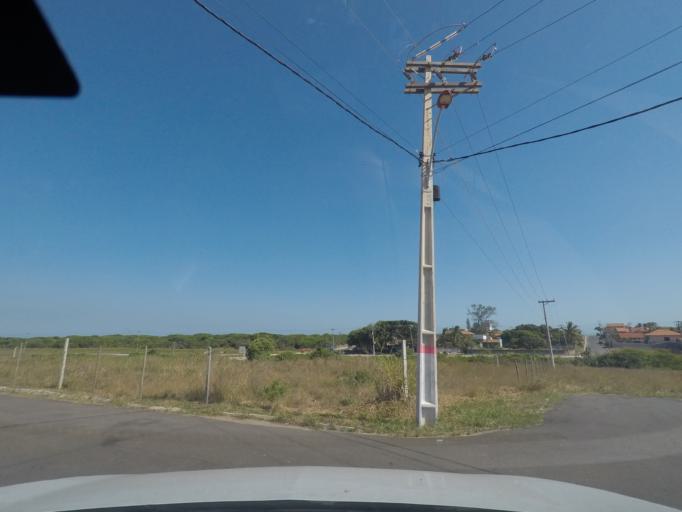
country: BR
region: Rio de Janeiro
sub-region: Marica
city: Marica
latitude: -22.9686
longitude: -42.9047
